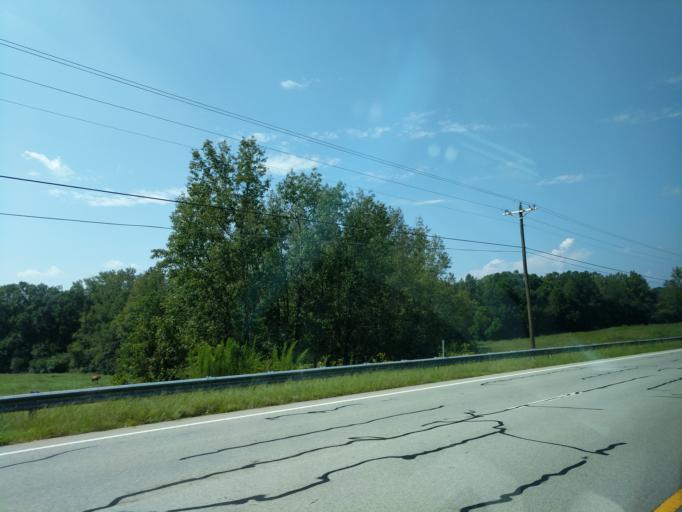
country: US
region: Georgia
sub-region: Franklin County
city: Lavonia
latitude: 34.4447
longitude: -83.0357
